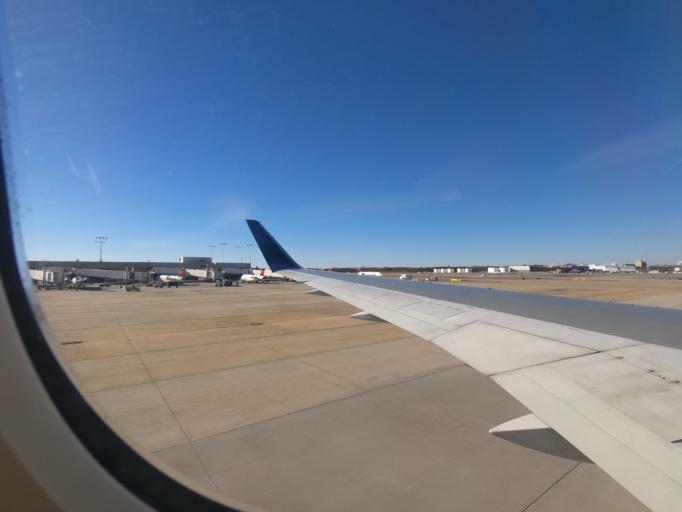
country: US
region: Georgia
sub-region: Fulton County
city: Hapeville
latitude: 33.6428
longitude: -84.4273
